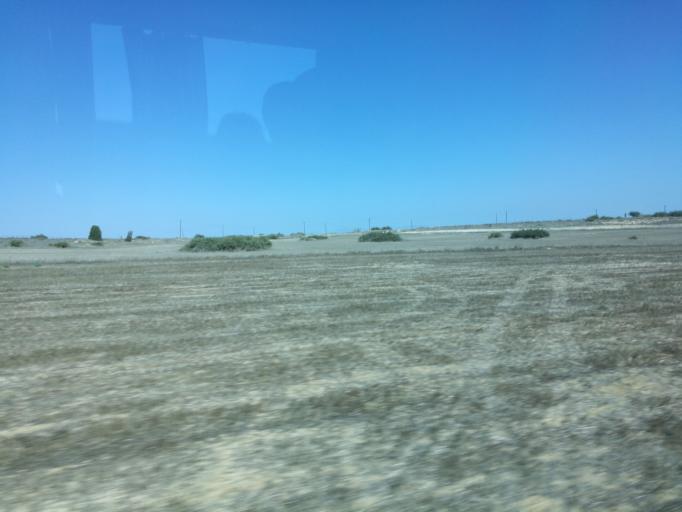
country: CY
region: Ammochostos
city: Acheritou
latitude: 35.0733
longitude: 33.8636
